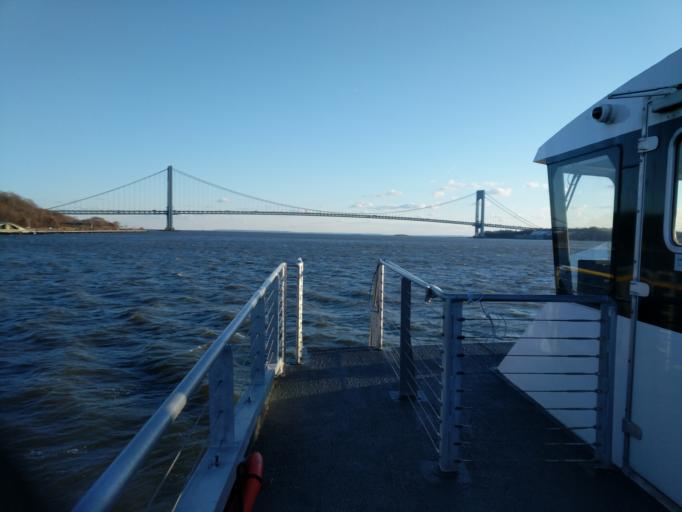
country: US
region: New York
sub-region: Kings County
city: Bensonhurst
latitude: 40.6239
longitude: -74.0441
